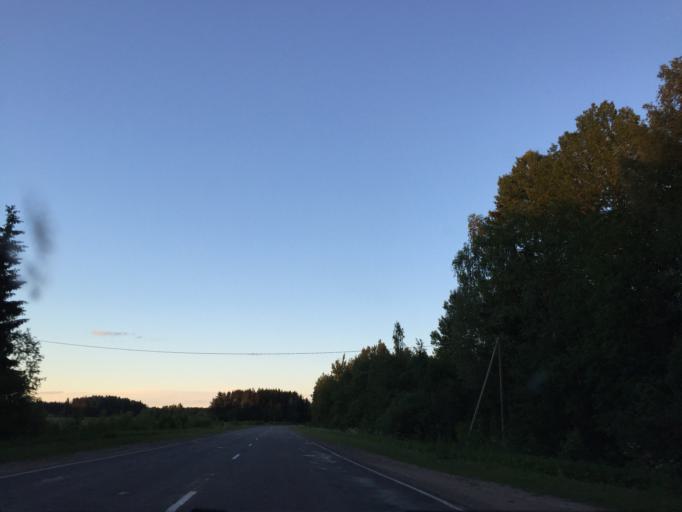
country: LV
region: Smiltene
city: Smiltene
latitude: 57.4385
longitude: 26.1797
